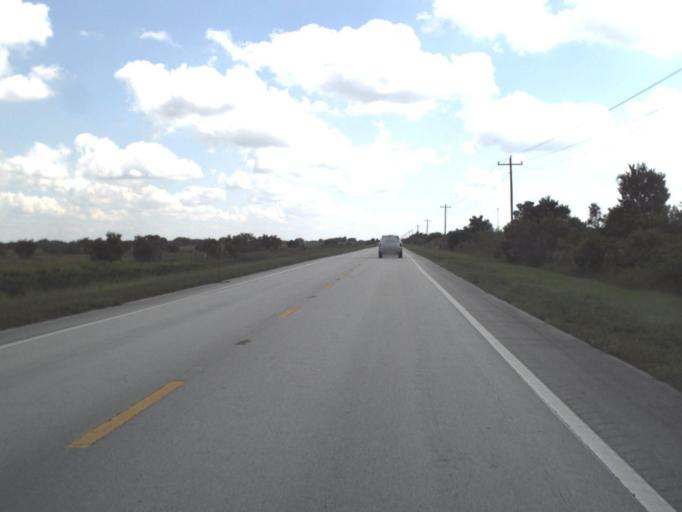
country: US
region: Florida
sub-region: Highlands County
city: Lake Placid
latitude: 27.4312
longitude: -81.2265
